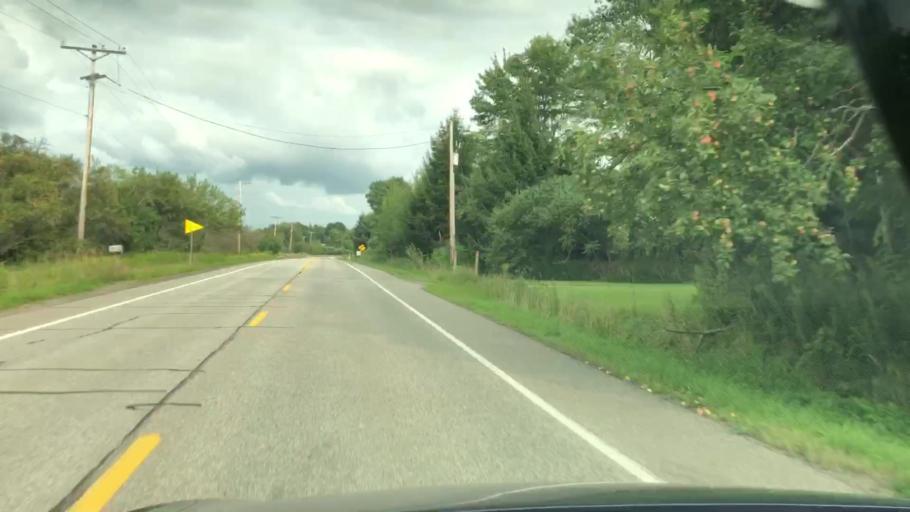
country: US
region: Pennsylvania
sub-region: Erie County
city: Union City
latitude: 42.0577
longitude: -79.8608
